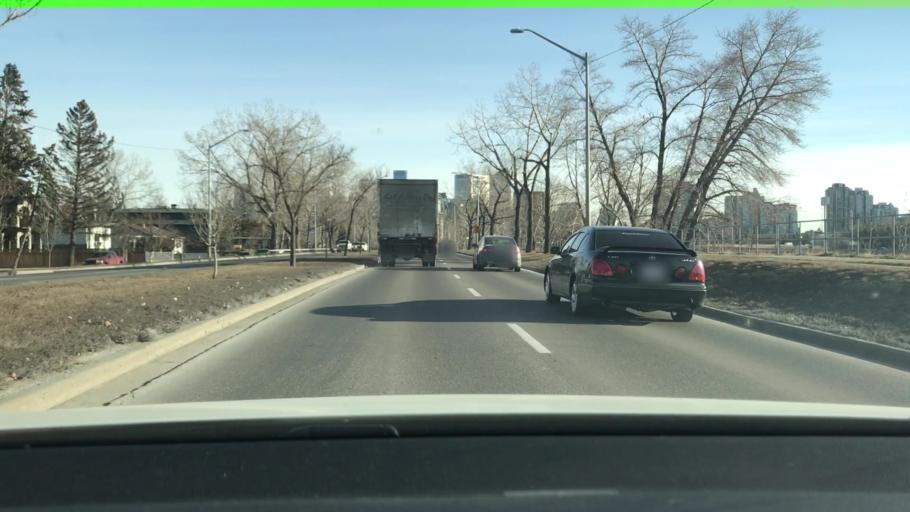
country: CA
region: Alberta
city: Calgary
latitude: 51.0490
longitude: -114.1041
